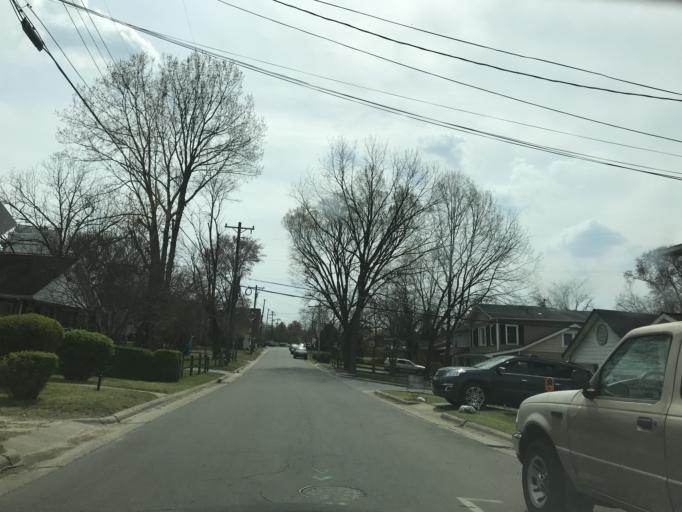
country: US
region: North Carolina
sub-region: Orange County
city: Carrboro
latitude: 35.9126
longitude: -79.0663
